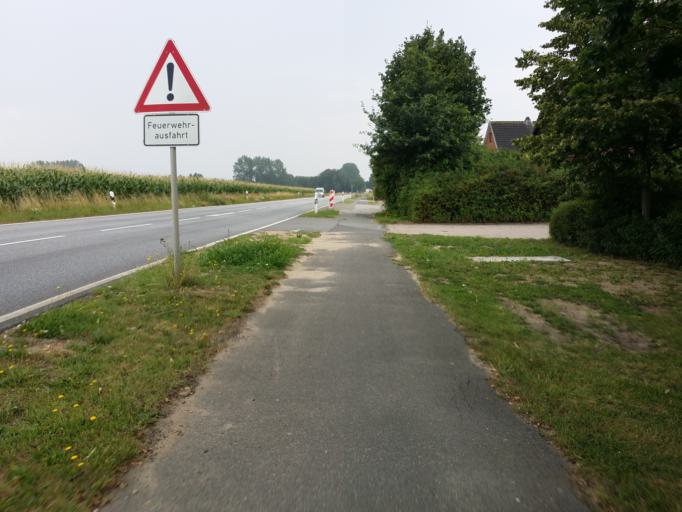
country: DE
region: Schleswig-Holstein
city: Blomesche Wildnis
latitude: 53.8111
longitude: 9.4254
